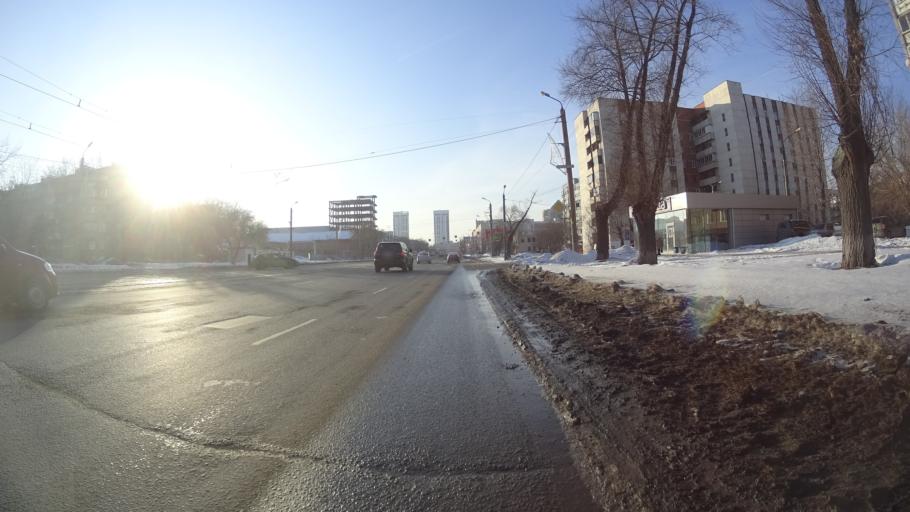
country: RU
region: Chelyabinsk
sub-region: Gorod Chelyabinsk
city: Chelyabinsk
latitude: 55.1682
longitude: 61.4244
